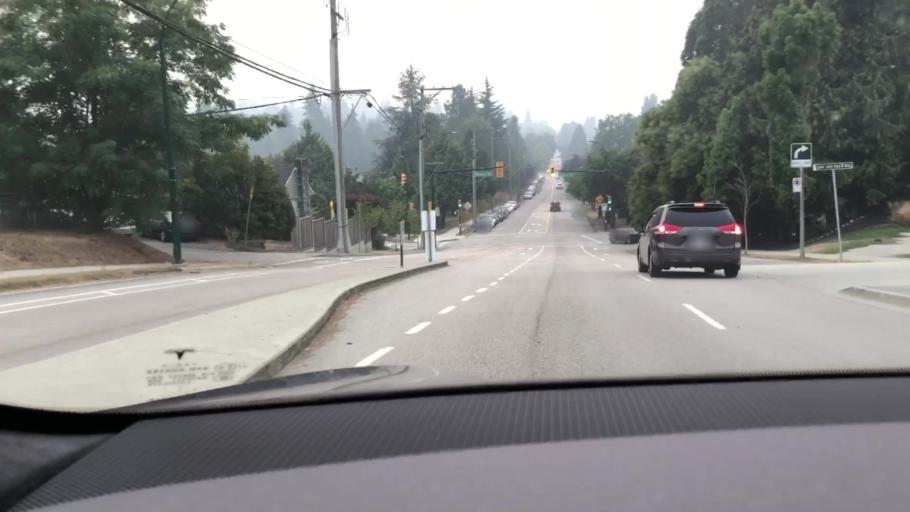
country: CA
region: British Columbia
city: Vancouver
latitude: 49.2412
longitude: -123.1225
